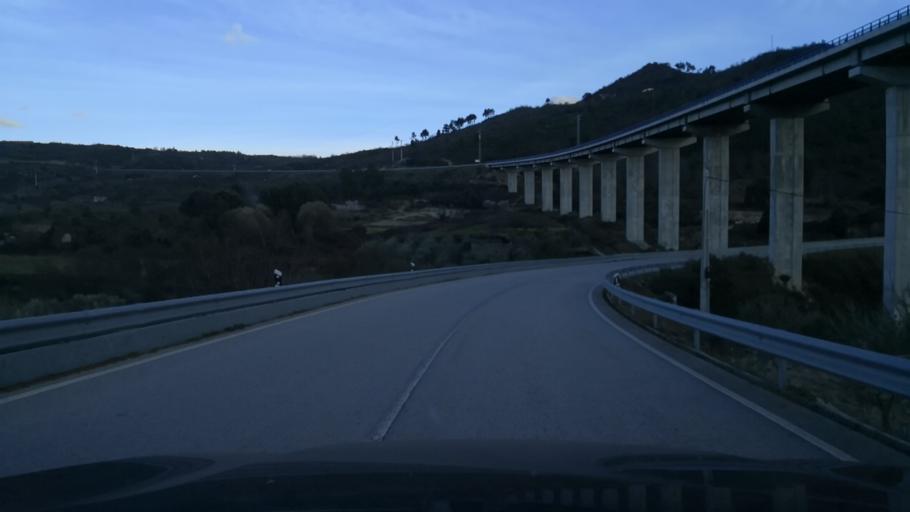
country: PT
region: Braganca
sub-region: Carrazeda de Ansiaes
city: Carrazeda de Anciaes
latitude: 41.2714
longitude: -7.3220
